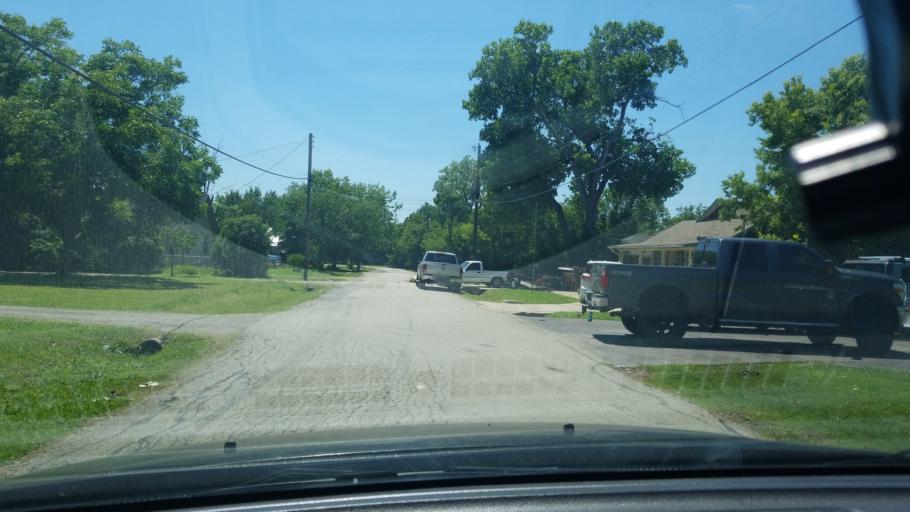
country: US
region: Texas
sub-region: Dallas County
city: Mesquite
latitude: 32.7653
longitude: -96.6064
